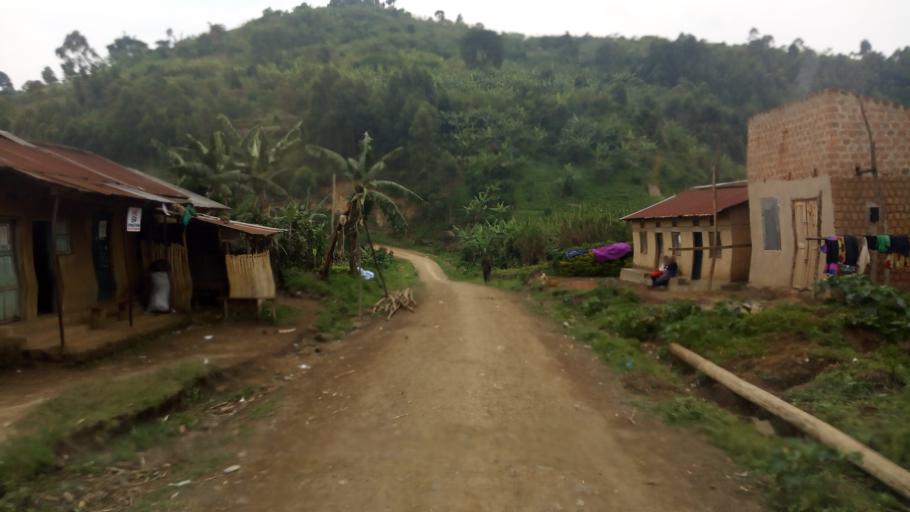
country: UG
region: Western Region
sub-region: Kisoro District
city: Kisoro
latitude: -1.2599
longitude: 29.6296
